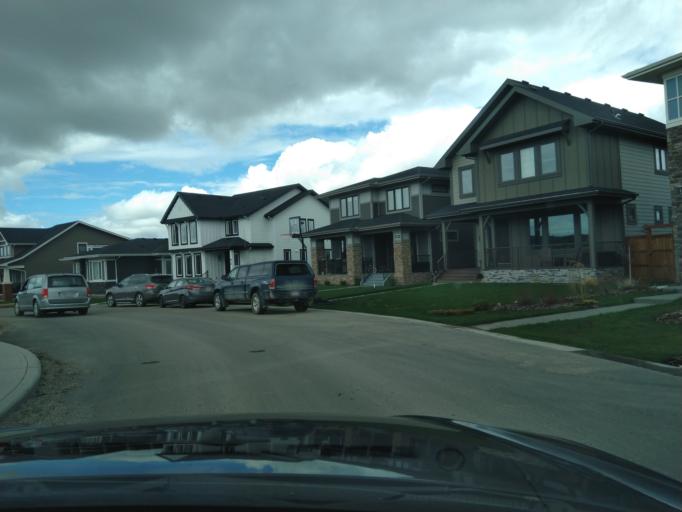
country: CA
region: Alberta
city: Cochrane
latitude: 51.1114
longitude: -114.3942
